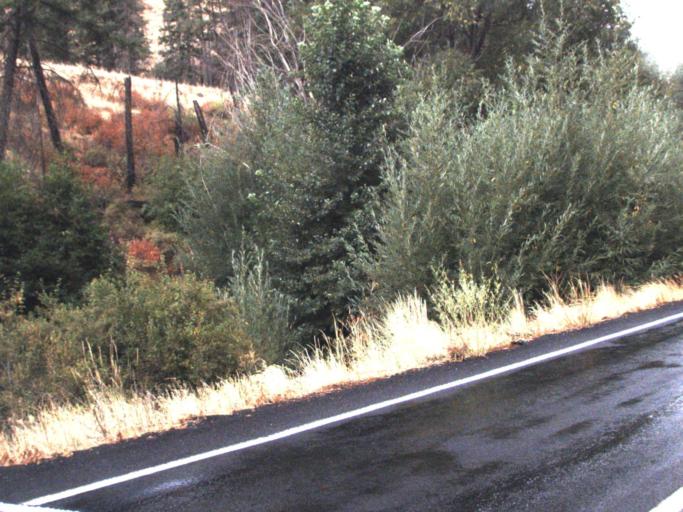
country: US
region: Washington
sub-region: Spokane County
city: Medical Lake
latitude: 47.7491
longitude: -117.8872
